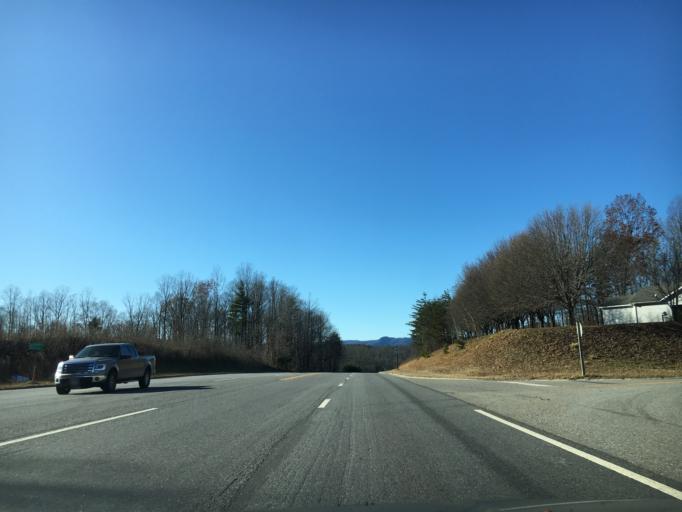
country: US
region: Virginia
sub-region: Patrick County
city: Patrick Springs
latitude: 36.6355
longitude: -80.2088
